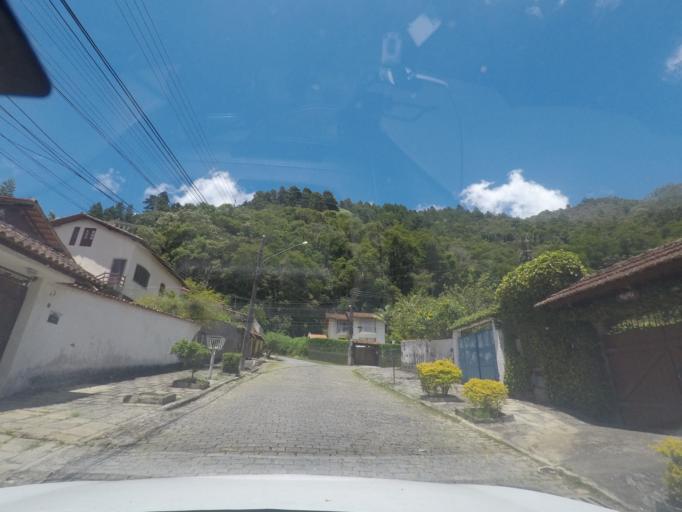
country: BR
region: Rio de Janeiro
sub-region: Teresopolis
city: Teresopolis
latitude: -22.4315
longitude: -42.9826
